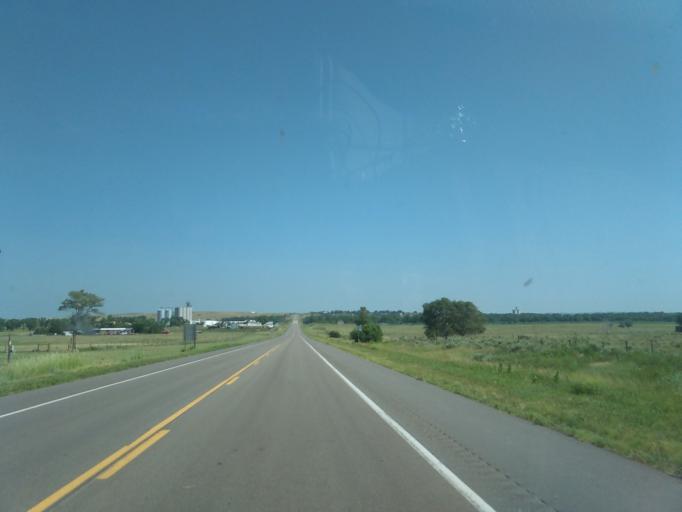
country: US
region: Nebraska
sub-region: Dundy County
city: Benkelman
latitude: 40.0250
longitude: -101.5428
